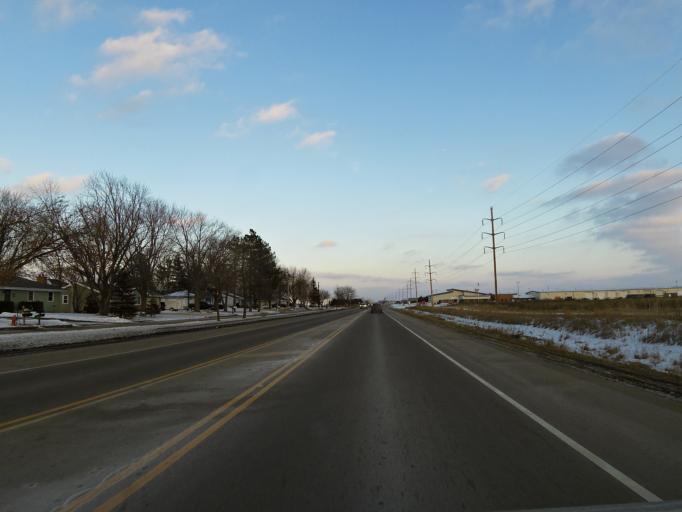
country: US
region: Minnesota
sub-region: Dakota County
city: Lakeville
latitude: 44.6379
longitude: -93.2519
